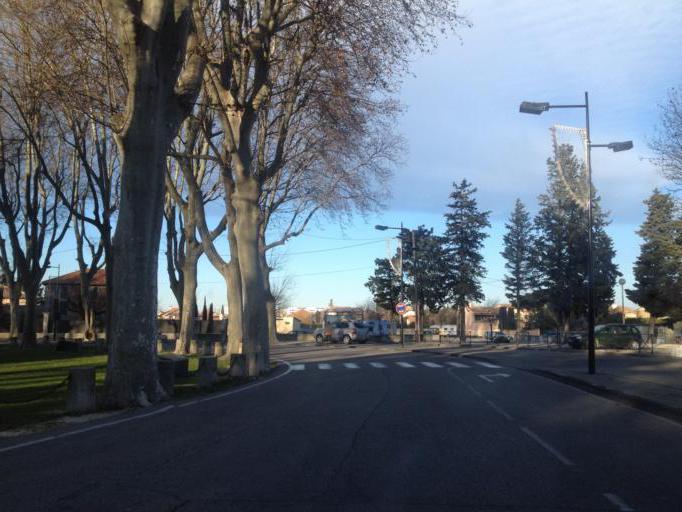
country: FR
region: Provence-Alpes-Cote d'Azur
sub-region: Departement du Vaucluse
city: Orange
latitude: 44.1419
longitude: 4.8052
